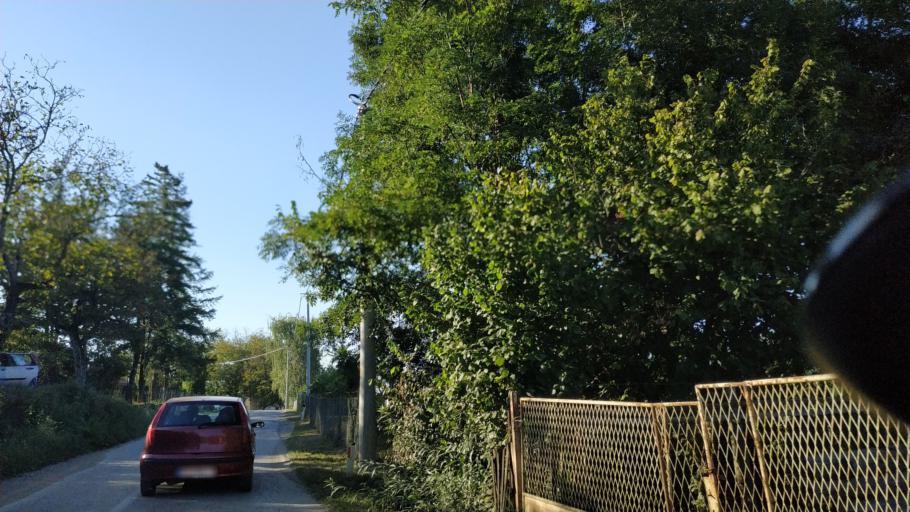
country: RS
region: Central Serbia
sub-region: Rasinski Okrug
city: Krusevac
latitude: 43.4926
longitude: 21.3442
